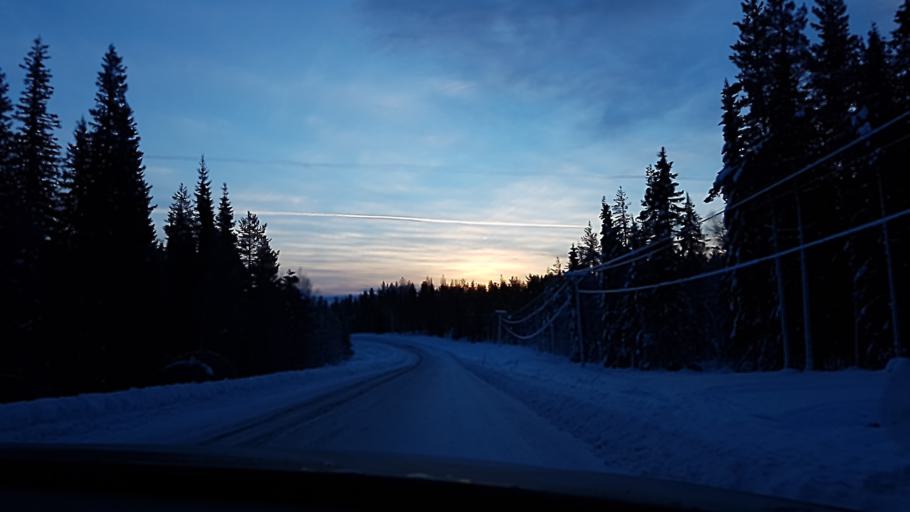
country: SE
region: Norrbotten
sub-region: Jokkmokks Kommun
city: Jokkmokk
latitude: 66.1309
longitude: 20.0026
